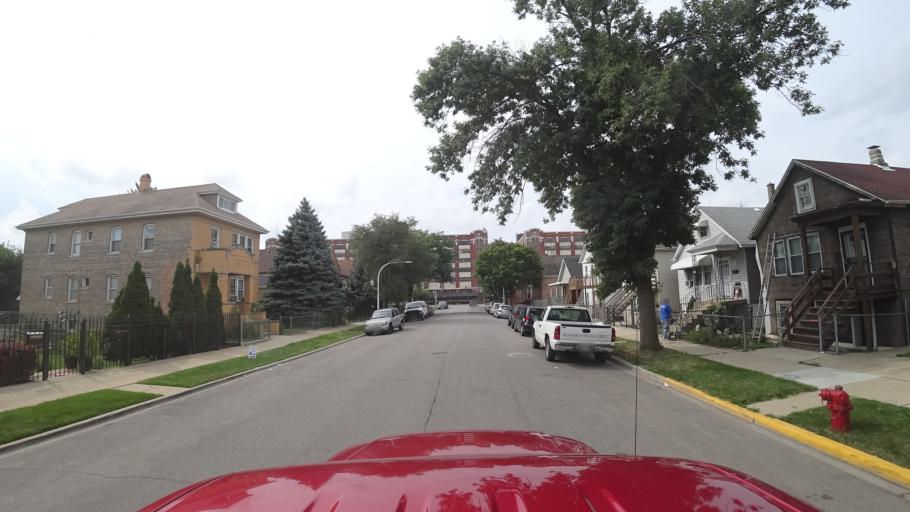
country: US
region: Illinois
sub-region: Cook County
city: Chicago
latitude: 41.8242
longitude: -87.6702
